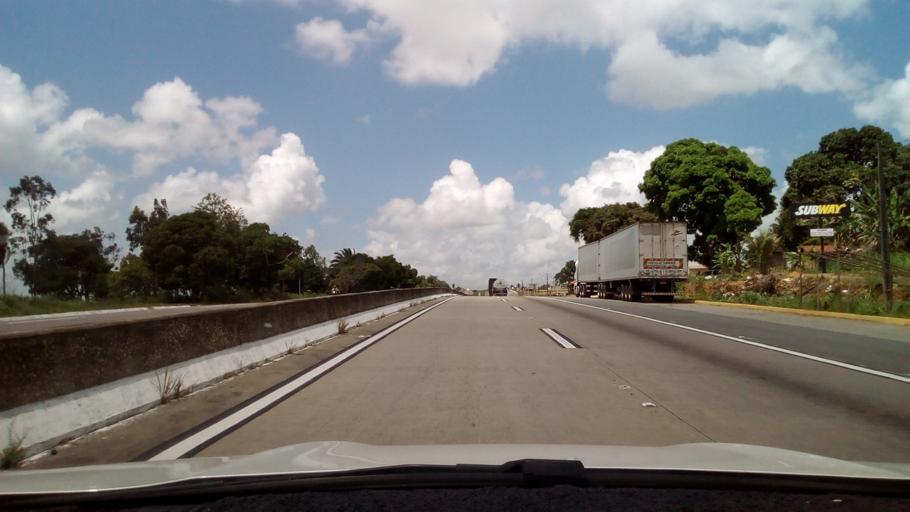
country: BR
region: Paraiba
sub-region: Alhandra
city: Alhandra
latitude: -7.3655
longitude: -34.9529
